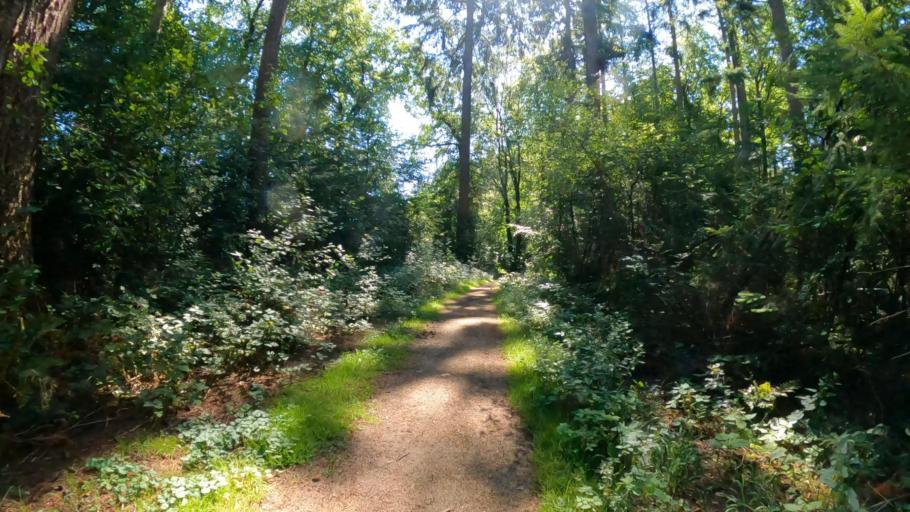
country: DE
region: Schleswig-Holstein
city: Kroppelshagen-Fahrendorf
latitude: 53.4794
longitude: 10.3486
